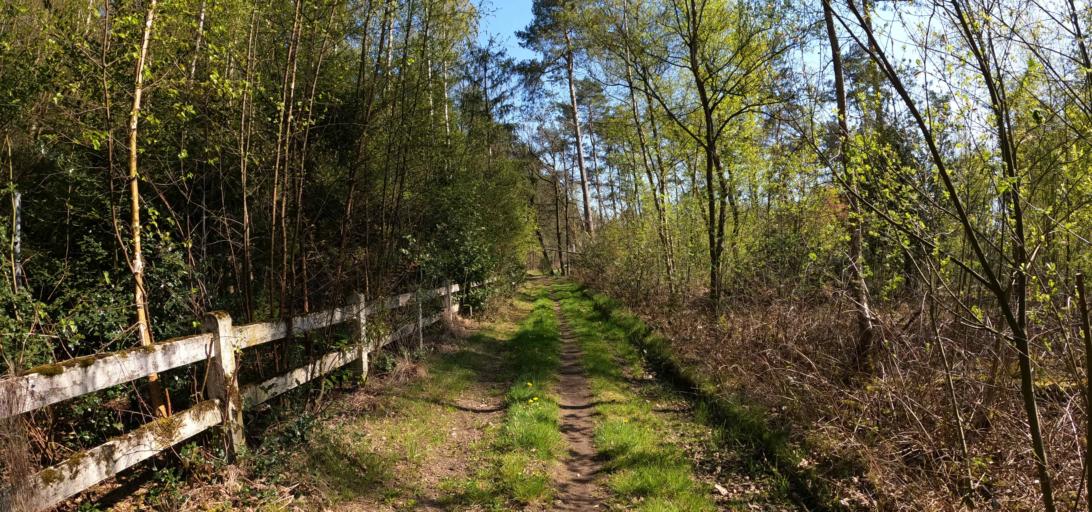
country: BE
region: Flanders
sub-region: Provincie Antwerpen
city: Vorselaar
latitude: 51.2316
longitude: 4.7616
